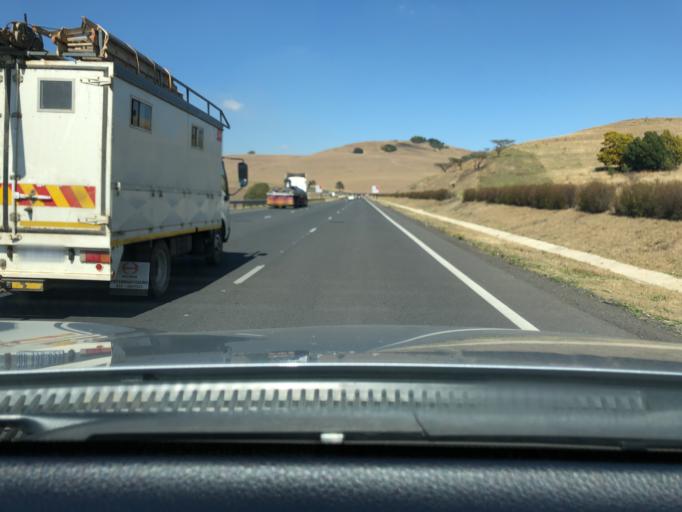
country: ZA
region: KwaZulu-Natal
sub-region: uThukela District Municipality
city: Estcourt
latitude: -29.0991
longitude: 29.9414
